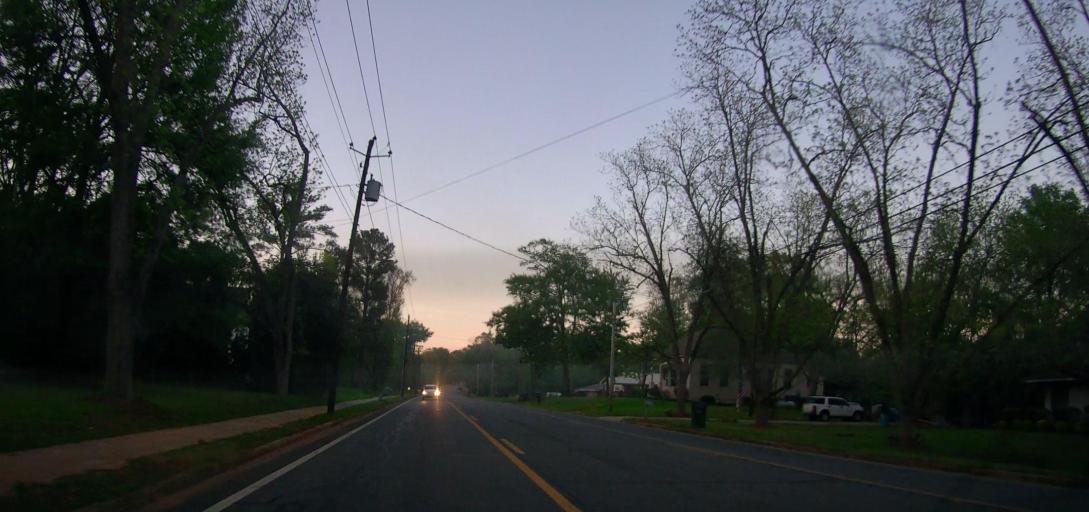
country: US
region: Georgia
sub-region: Marion County
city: Buena Vista
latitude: 32.3112
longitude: -84.5207
